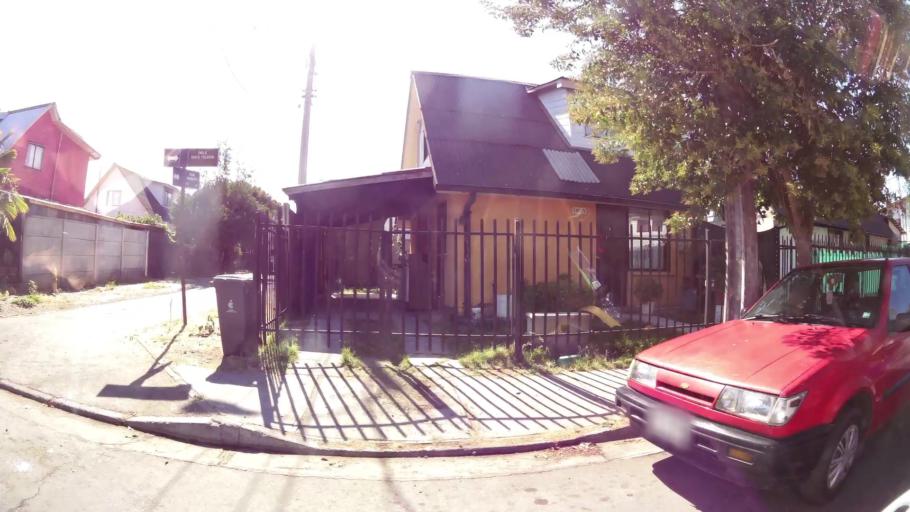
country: CL
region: Maule
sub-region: Provincia de Curico
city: Curico
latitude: -34.9788
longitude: -71.2672
